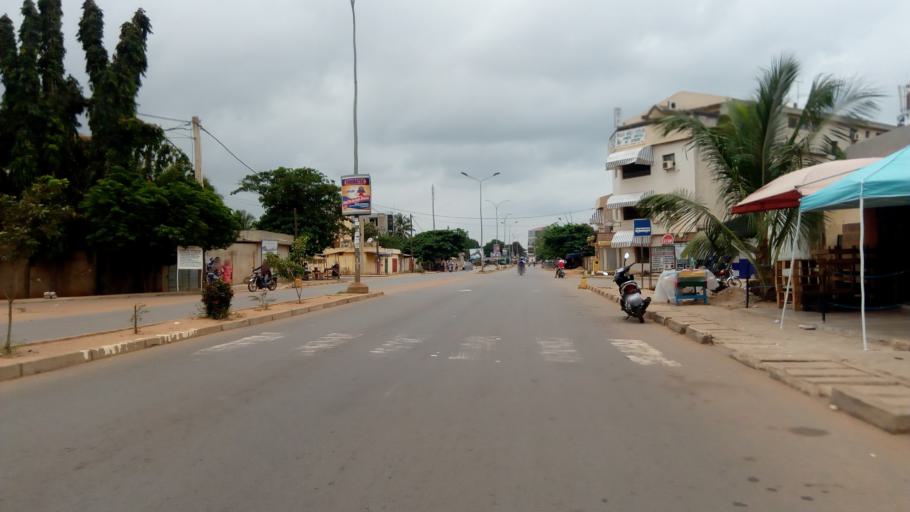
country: TG
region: Maritime
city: Lome
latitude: 6.2191
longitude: 1.2044
